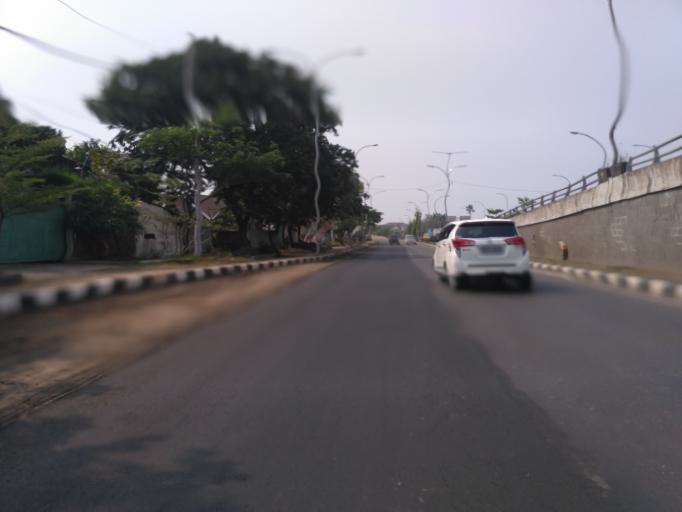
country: ID
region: Central Java
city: Semarang
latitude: -6.9831
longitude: 110.3852
